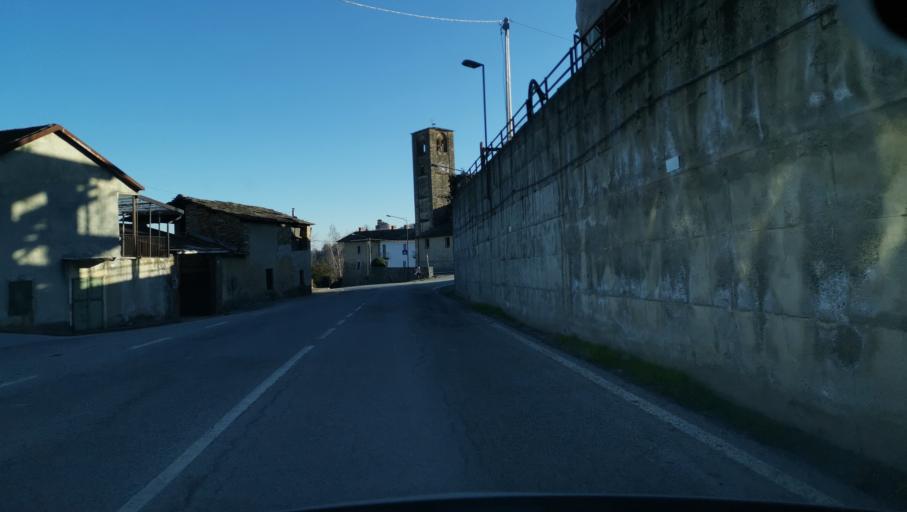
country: IT
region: Piedmont
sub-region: Provincia di Cuneo
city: Bagnolo Piemonte
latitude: 44.7536
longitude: 7.2898
